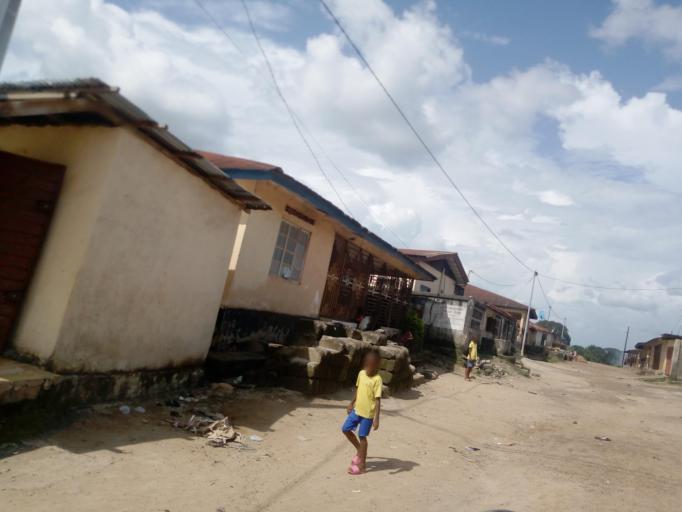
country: SL
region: Northern Province
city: Makeni
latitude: 8.8884
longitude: -12.0370
